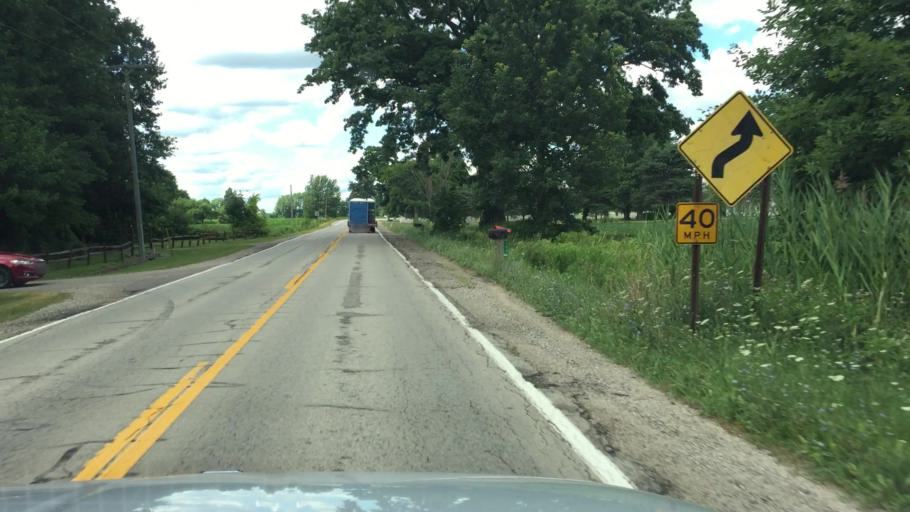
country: US
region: Michigan
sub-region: Saint Clair County
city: Capac
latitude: 42.9410
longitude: -82.9460
